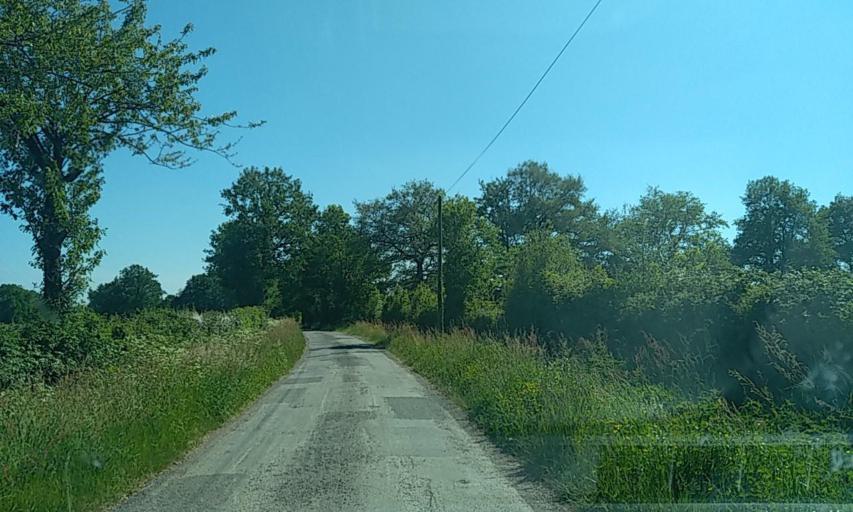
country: FR
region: Poitou-Charentes
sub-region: Departement des Deux-Sevres
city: Boisme
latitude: 46.7985
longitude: -0.4638
